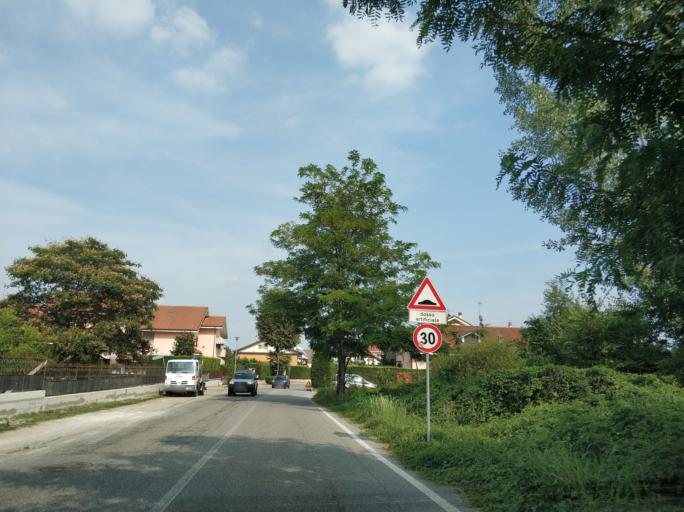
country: IT
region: Piedmont
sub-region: Provincia di Torino
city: Leini
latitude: 45.1503
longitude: 7.6951
